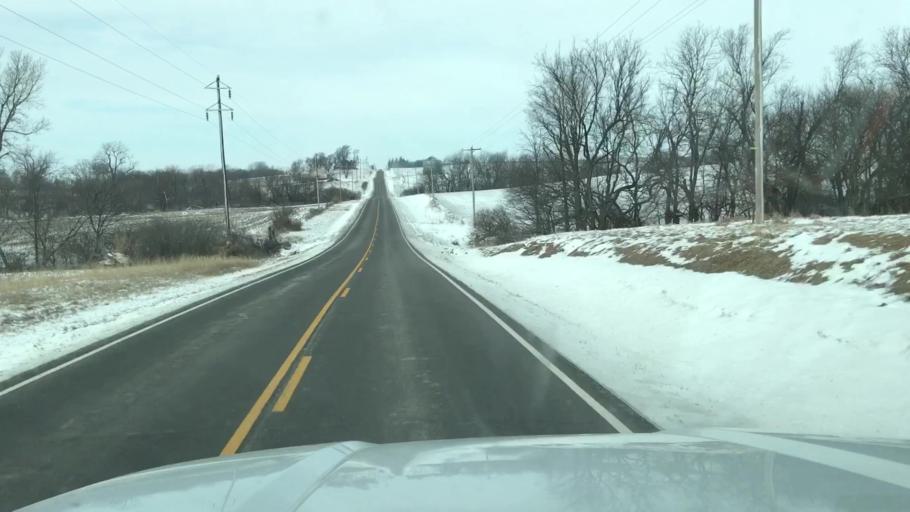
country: US
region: Missouri
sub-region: Holt County
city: Mound City
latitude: 40.1301
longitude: -95.1113
